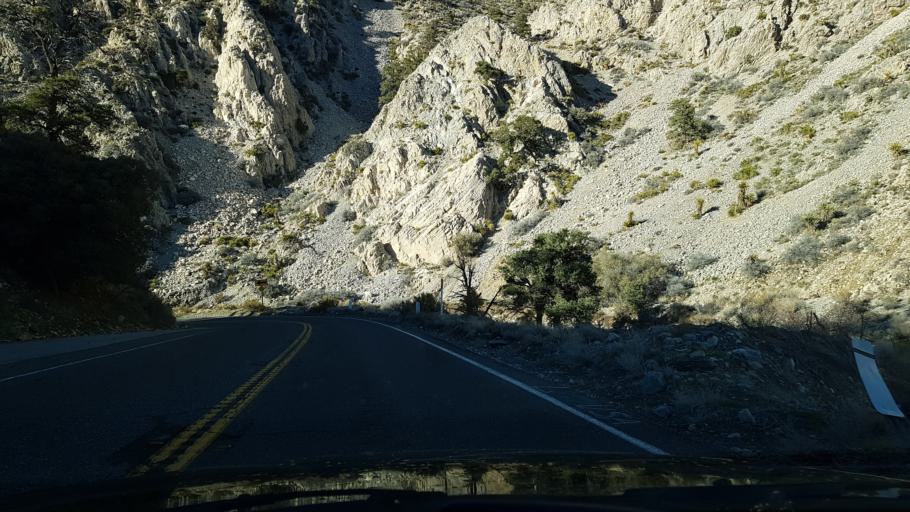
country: US
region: California
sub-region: San Bernardino County
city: Big Bear City
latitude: 34.3372
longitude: -116.8344
